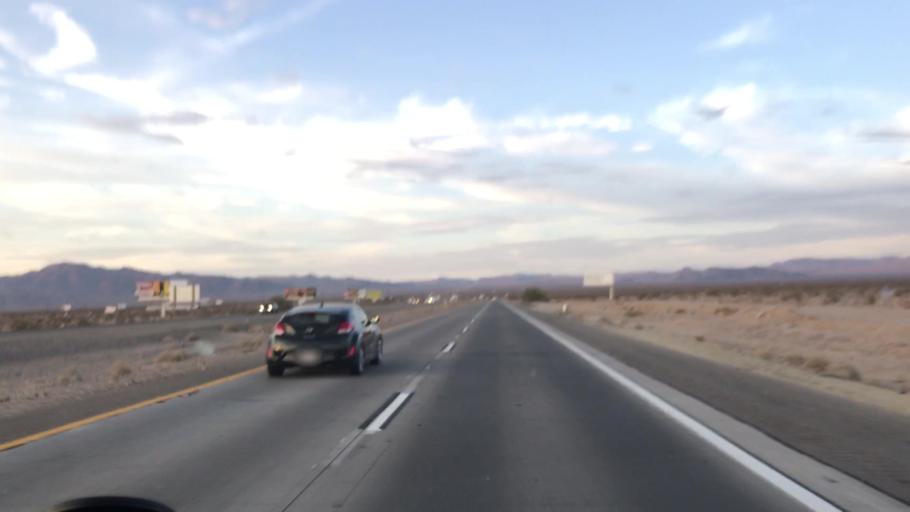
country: US
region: California
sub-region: San Bernardino County
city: Fort Irwin
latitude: 35.2727
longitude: -116.0581
